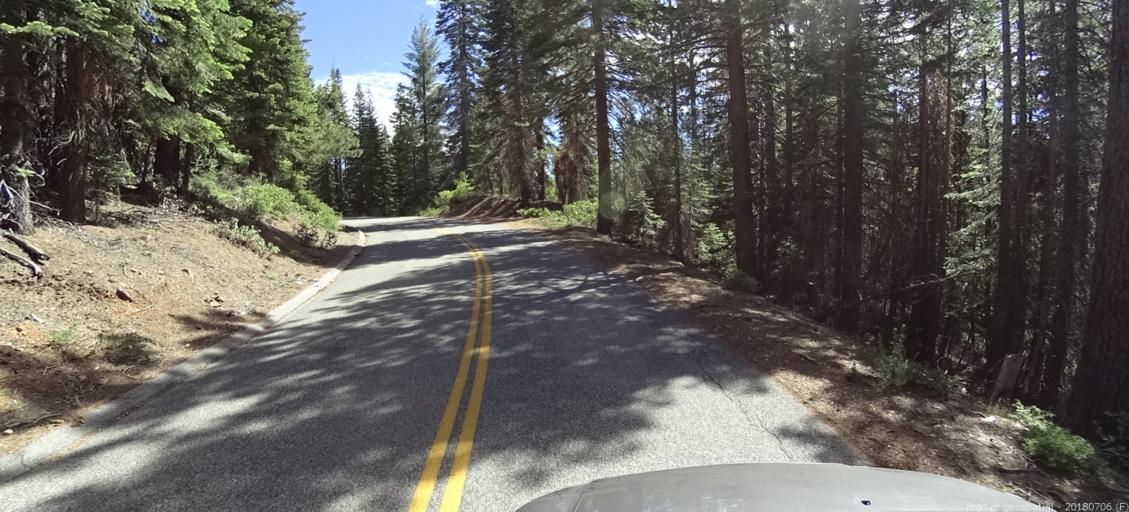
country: US
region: California
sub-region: Madera County
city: Oakhurst
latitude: 37.3937
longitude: -119.5188
